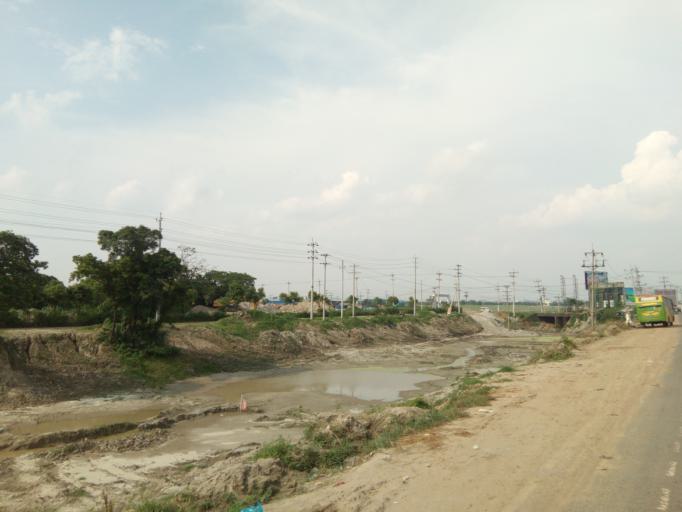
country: BD
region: Dhaka
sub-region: Dhaka
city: Dhaka
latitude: 23.6739
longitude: 90.4039
